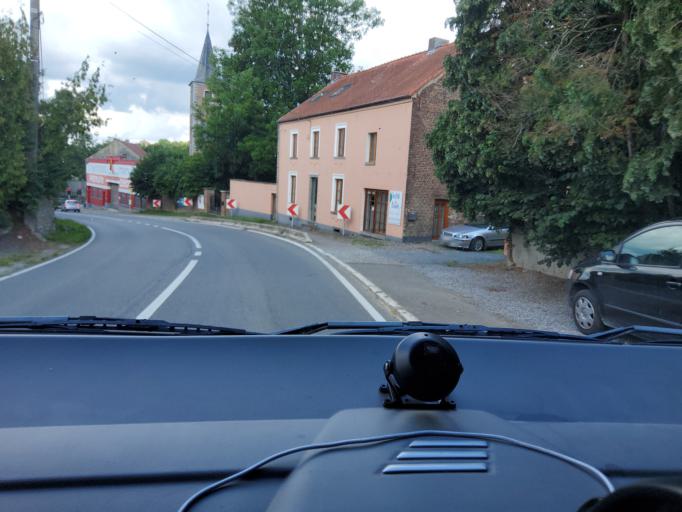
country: BE
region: Wallonia
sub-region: Province du Brabant Wallon
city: Genappe
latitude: 50.5813
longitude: 4.4174
